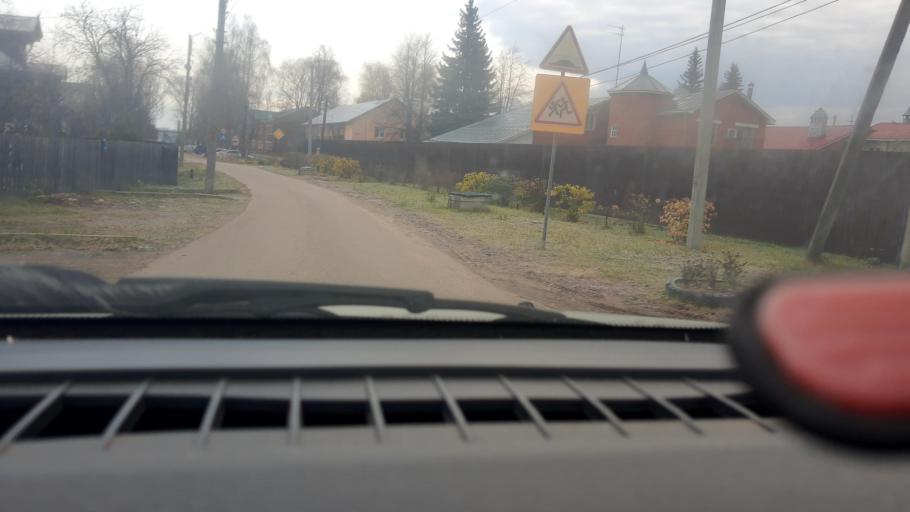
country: RU
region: Nizjnij Novgorod
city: Afonino
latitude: 56.2049
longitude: 44.1050
